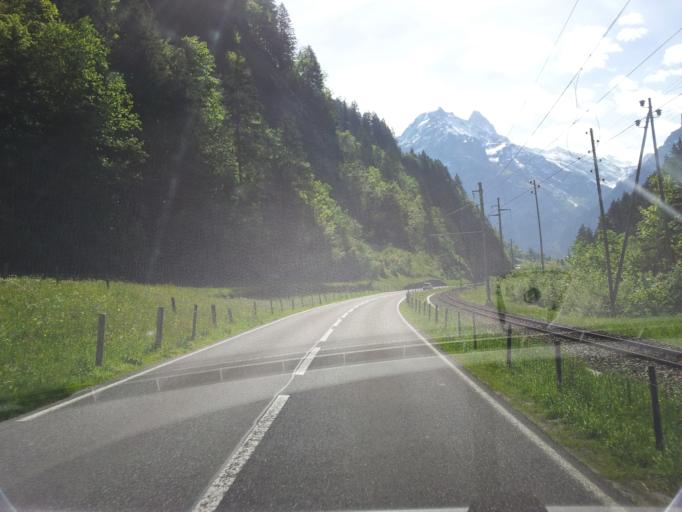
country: CH
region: Bern
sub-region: Interlaken-Oberhasli District
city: Grindelwald
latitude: 46.6357
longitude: 7.9928
